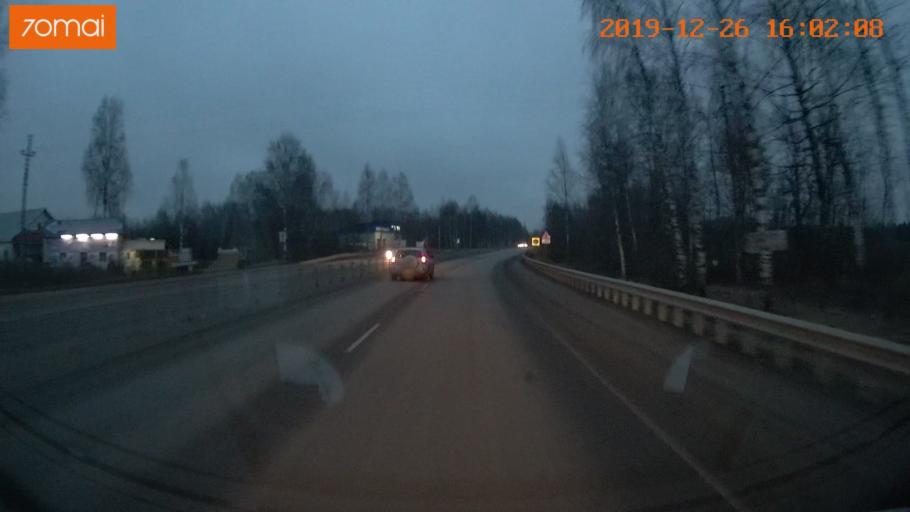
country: RU
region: Jaroslavl
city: Rybinsk
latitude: 58.0139
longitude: 38.8292
